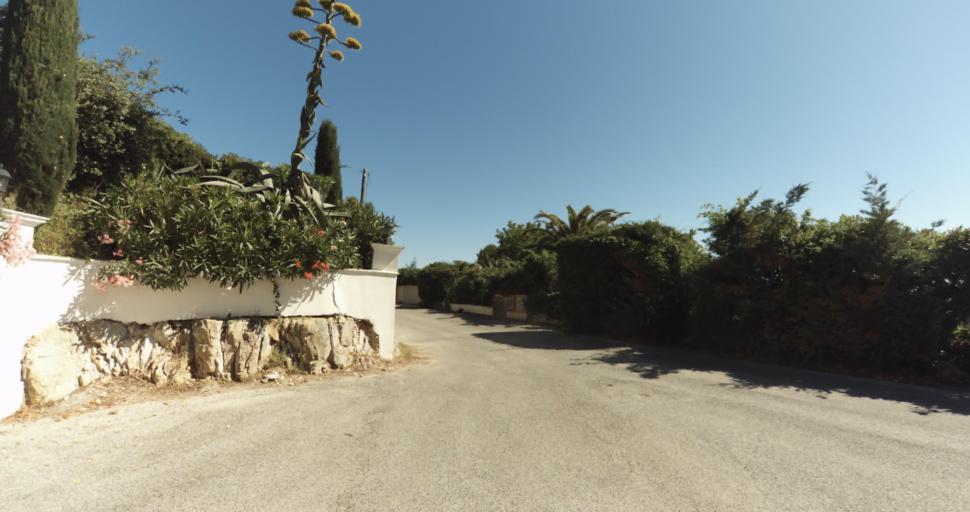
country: FR
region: Provence-Alpes-Cote d'Azur
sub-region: Departement du Var
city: Saint-Tropez
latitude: 43.2573
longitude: 6.6119
